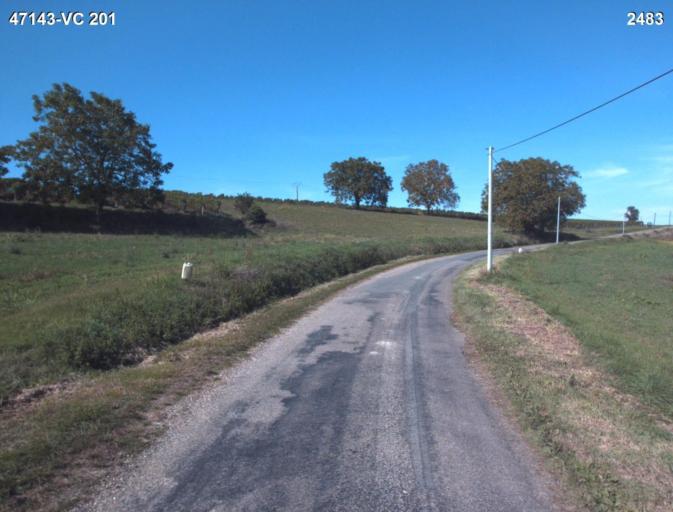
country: FR
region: Aquitaine
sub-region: Departement du Lot-et-Garonne
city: Vianne
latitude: 44.1807
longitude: 0.3340
